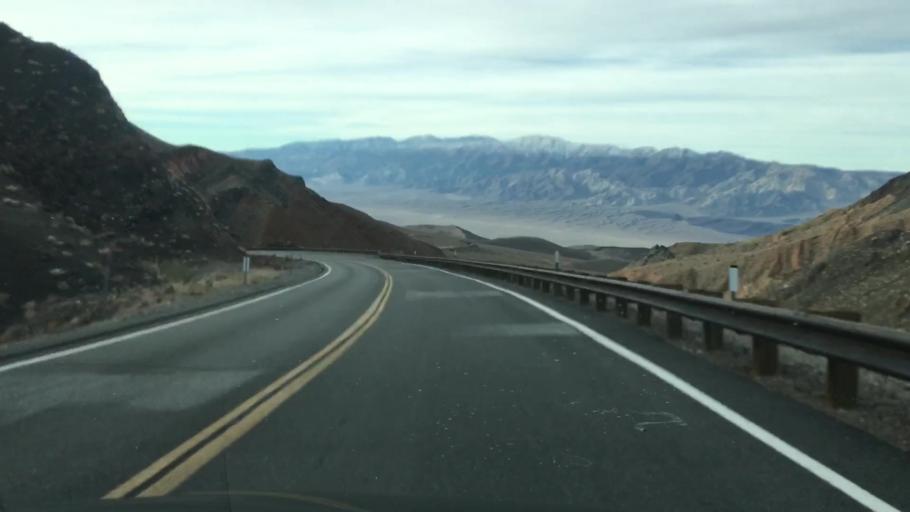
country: US
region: California
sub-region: San Bernardino County
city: Searles Valley
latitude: 36.3625
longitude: -117.2882
